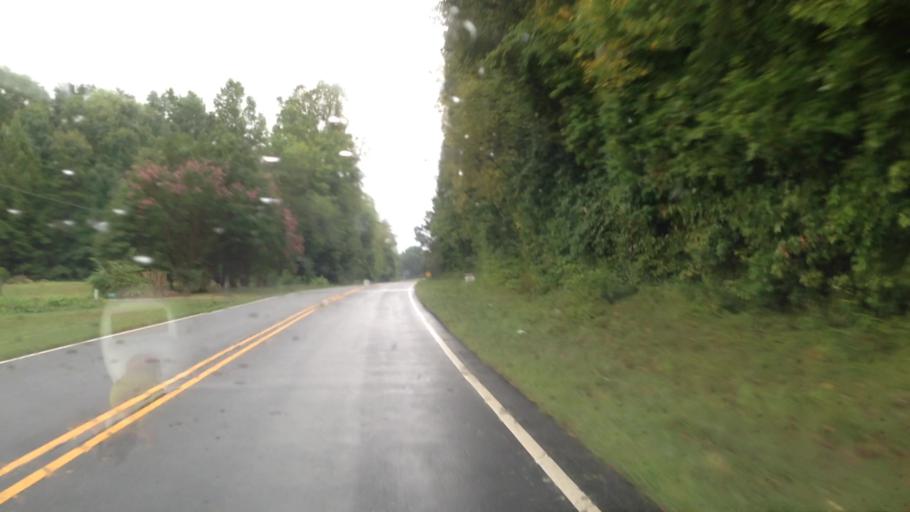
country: US
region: North Carolina
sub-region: Stokes County
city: Walnut Cove
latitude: 36.3792
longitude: -80.0918
